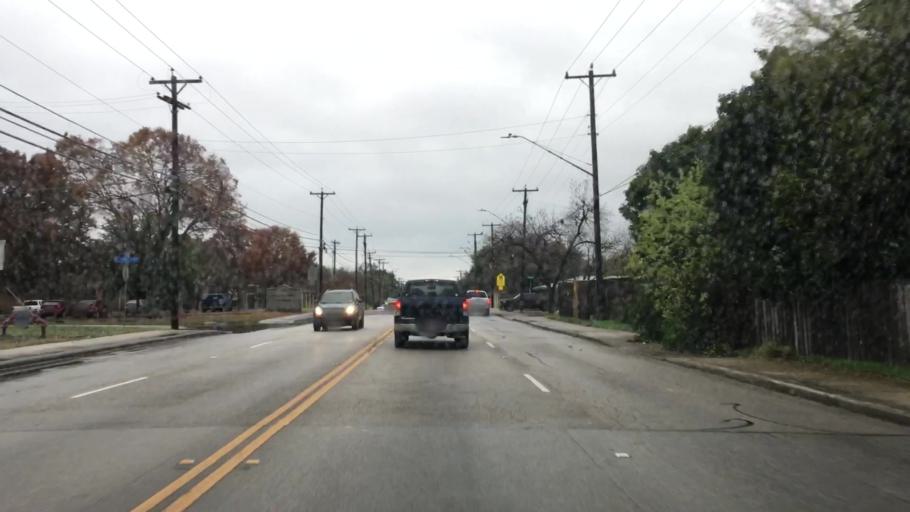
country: US
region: Texas
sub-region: Bexar County
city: Castle Hills
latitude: 29.5078
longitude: -98.5069
